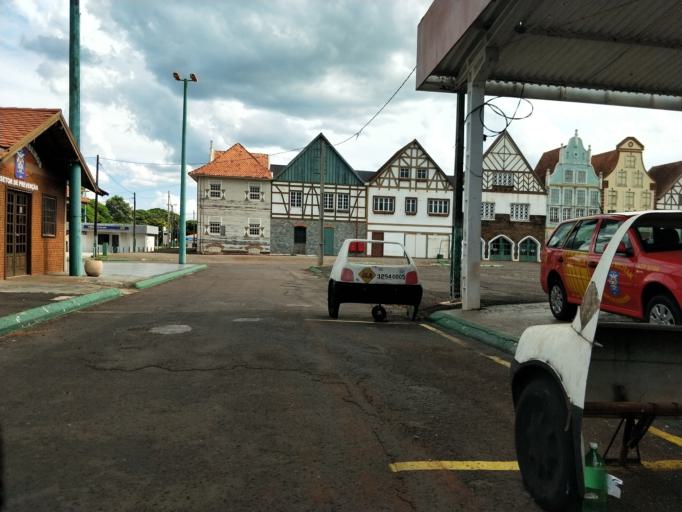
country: BR
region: Parana
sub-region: Marechal Candido Rondon
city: Marechal Candido Rondon
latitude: -24.5528
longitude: -54.0506
